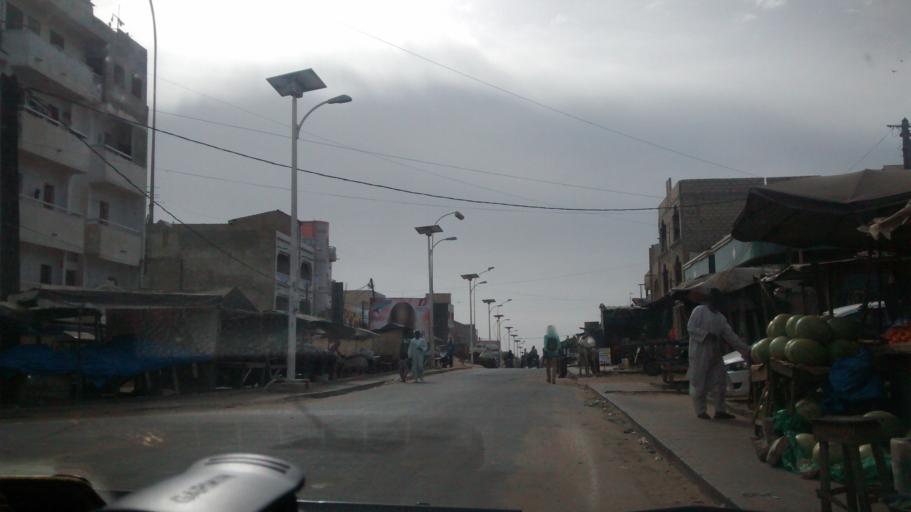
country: SN
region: Dakar
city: Pikine
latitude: 14.7794
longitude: -17.3801
